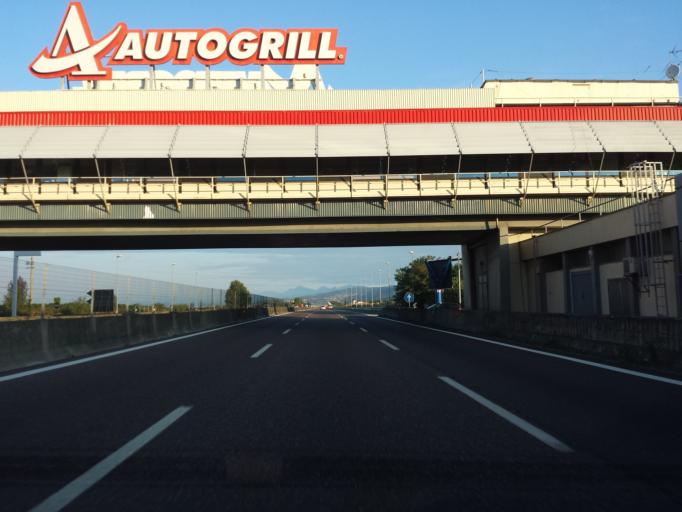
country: IT
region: Lombardy
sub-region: Provincia di Brescia
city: Erbusco
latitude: 45.5940
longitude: 9.9655
